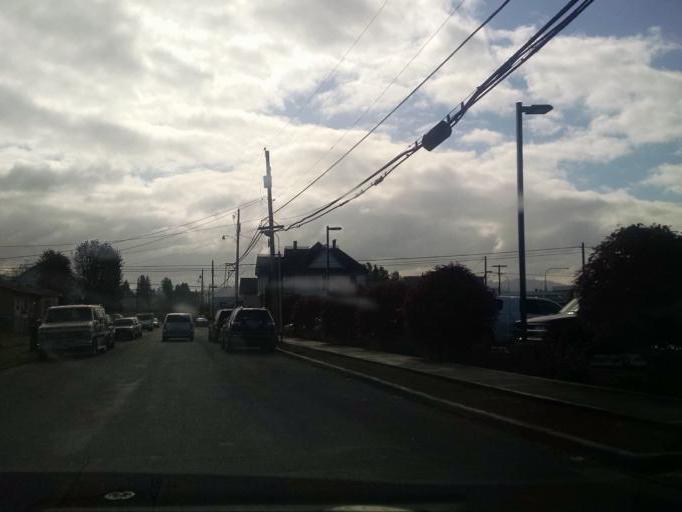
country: US
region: Washington
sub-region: Cowlitz County
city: Kelso
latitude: 46.1468
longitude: -122.9178
